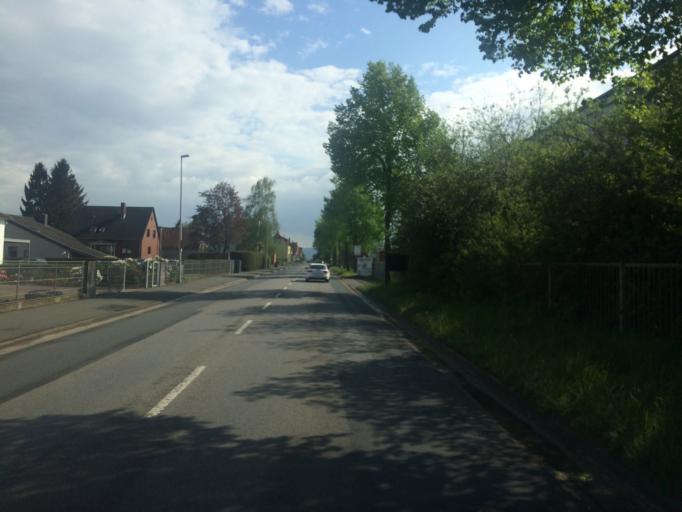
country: DE
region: Lower Saxony
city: Gross Munzel
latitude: 52.3706
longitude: 9.4794
